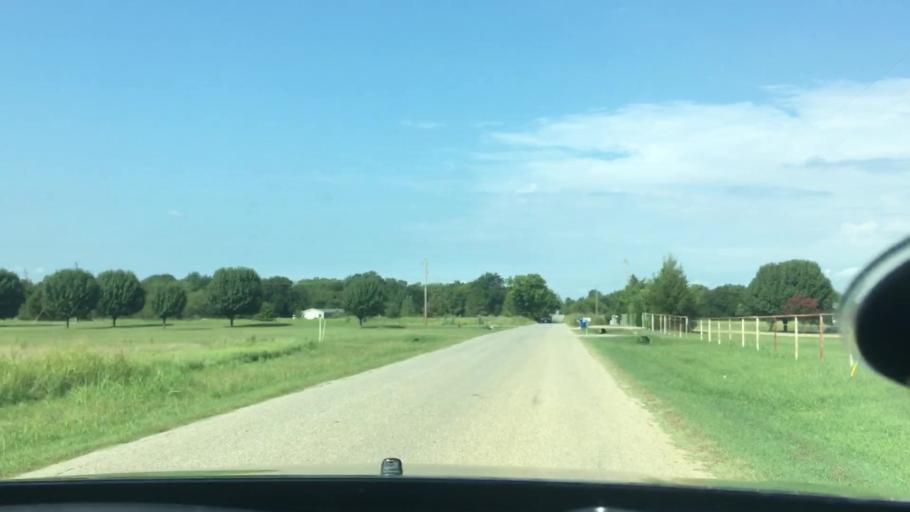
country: US
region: Oklahoma
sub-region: Bryan County
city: Calera
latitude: 33.9110
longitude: -96.4773
